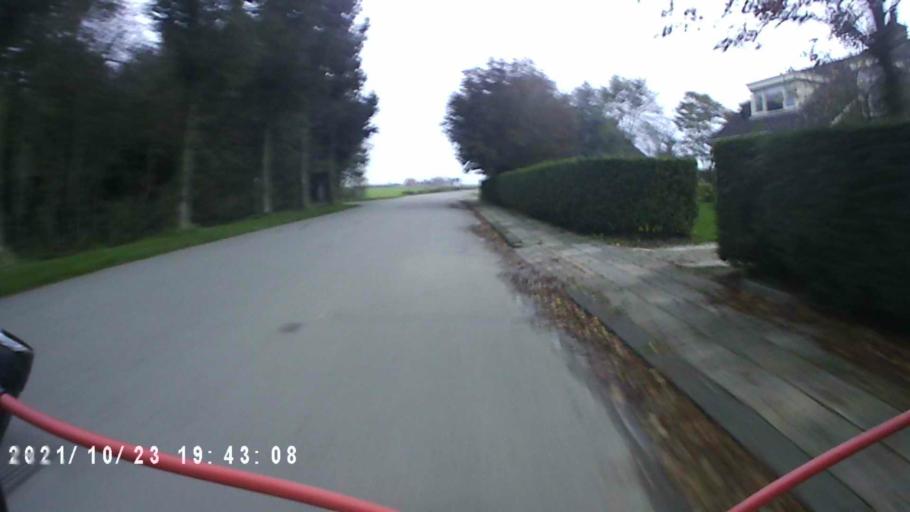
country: NL
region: Friesland
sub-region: Sudwest Fryslan
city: Makkum
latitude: 53.0828
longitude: 5.4252
